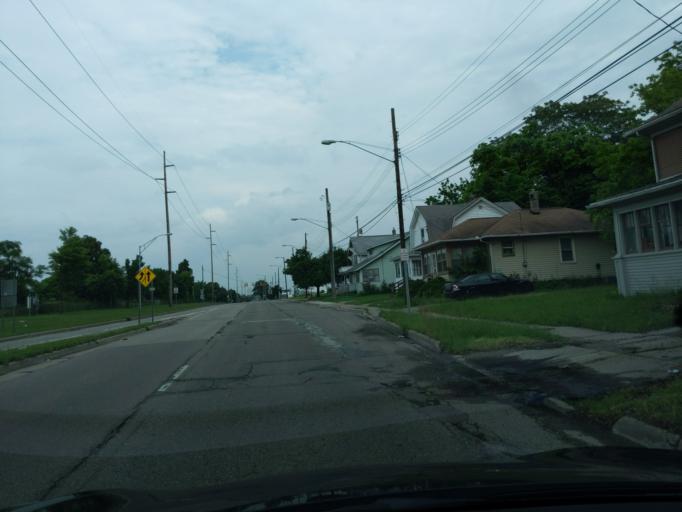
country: US
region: Michigan
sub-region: Ingham County
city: Lansing
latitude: 42.7256
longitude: -84.5722
